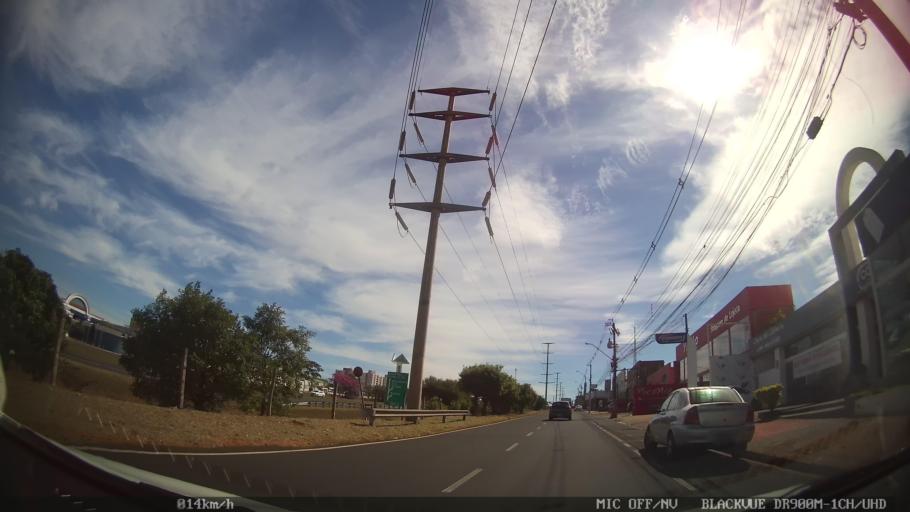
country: BR
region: Sao Paulo
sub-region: Sao Jose Do Rio Preto
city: Sao Jose do Rio Preto
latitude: -20.8370
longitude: -49.3556
